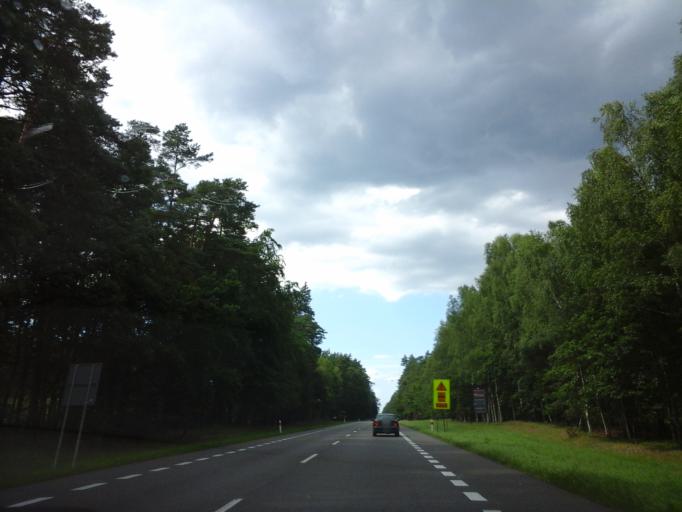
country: PL
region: West Pomeranian Voivodeship
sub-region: Powiat goleniowski
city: Przybiernow
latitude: 53.6924
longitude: 14.7936
